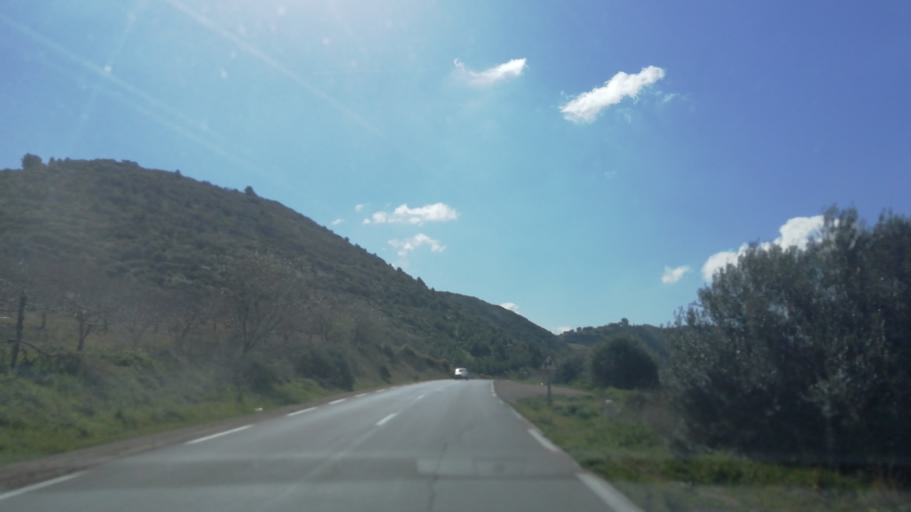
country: DZ
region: Mascara
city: Mascara
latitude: 35.4677
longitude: 0.1534
